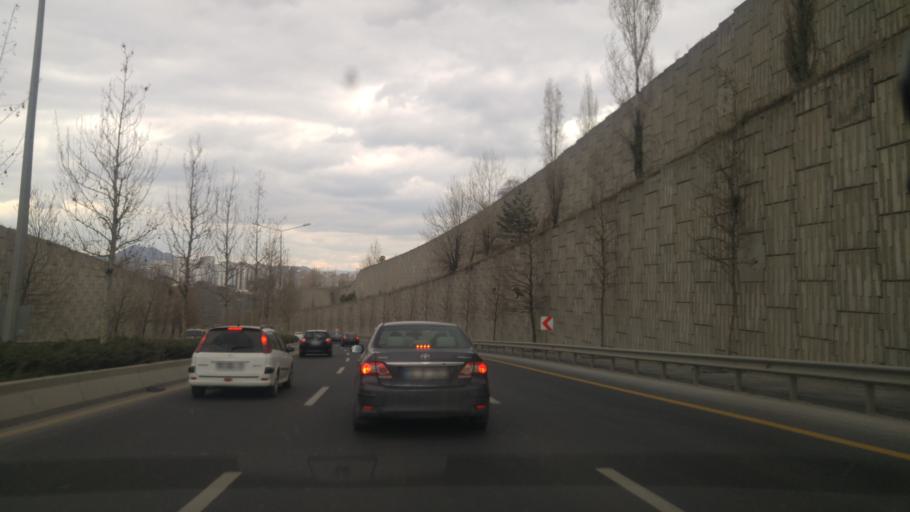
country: TR
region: Ankara
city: Cankaya
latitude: 39.8873
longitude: 32.8951
